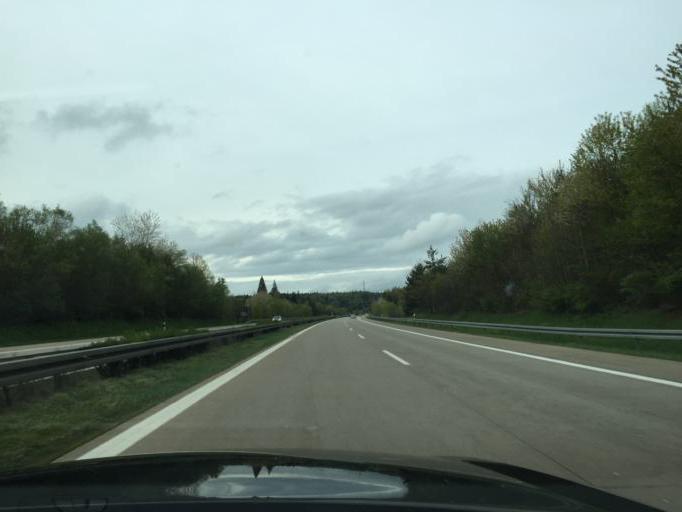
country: DE
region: Baden-Wuerttemberg
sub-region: Regierungsbezirk Stuttgart
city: Ellenberg
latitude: 49.0041
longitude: 10.1940
